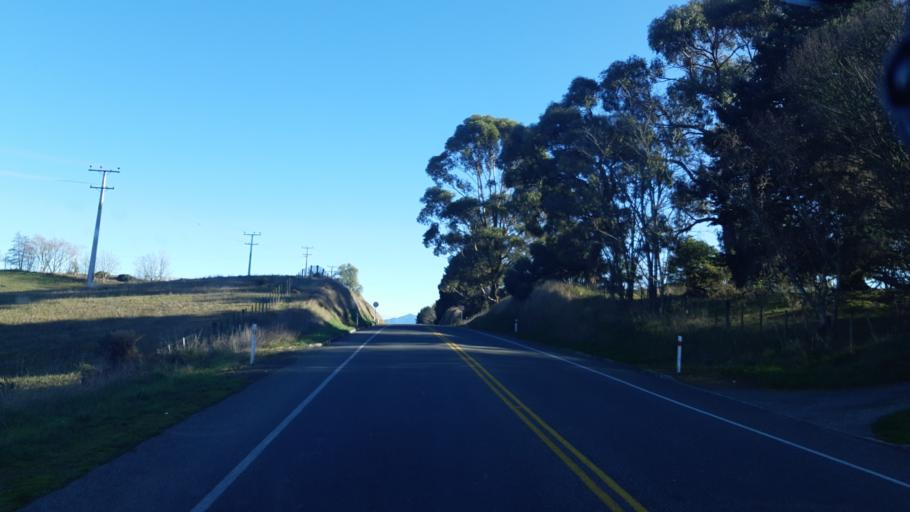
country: NZ
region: Tasman
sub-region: Tasman District
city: Mapua
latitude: -41.2980
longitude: 173.1039
